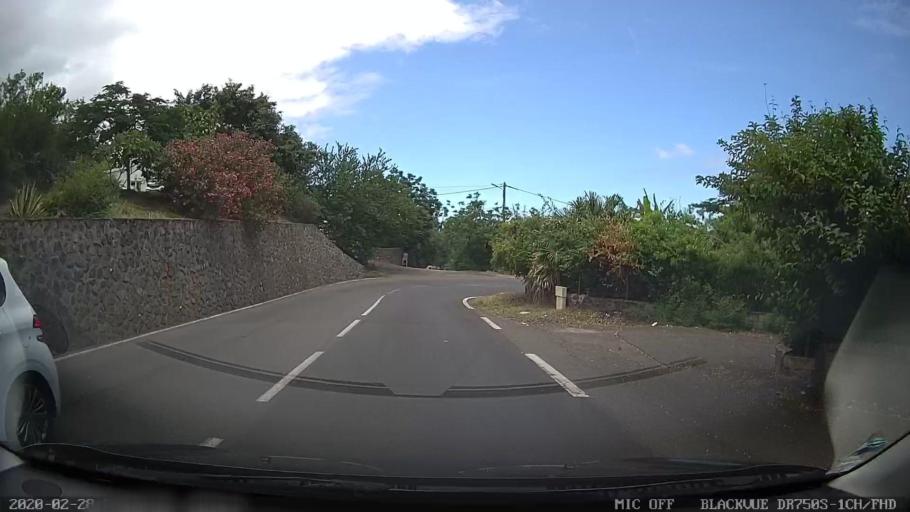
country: RE
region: Reunion
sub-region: Reunion
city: Saint-Leu
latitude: -21.1428
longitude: 55.2852
